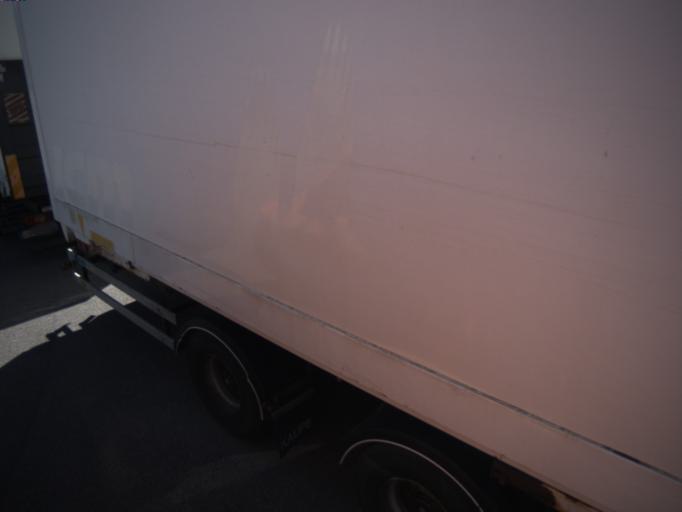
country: SE
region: Skane
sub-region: Helsingborg
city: Gantofta
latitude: 56.0157
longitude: 12.7690
